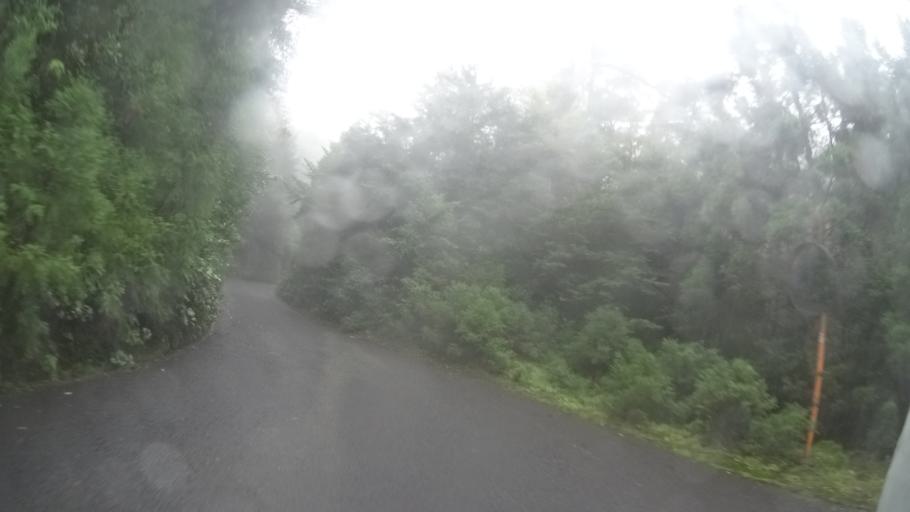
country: JP
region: Kagoshima
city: Nishinoomote
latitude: 30.2993
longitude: 130.5747
